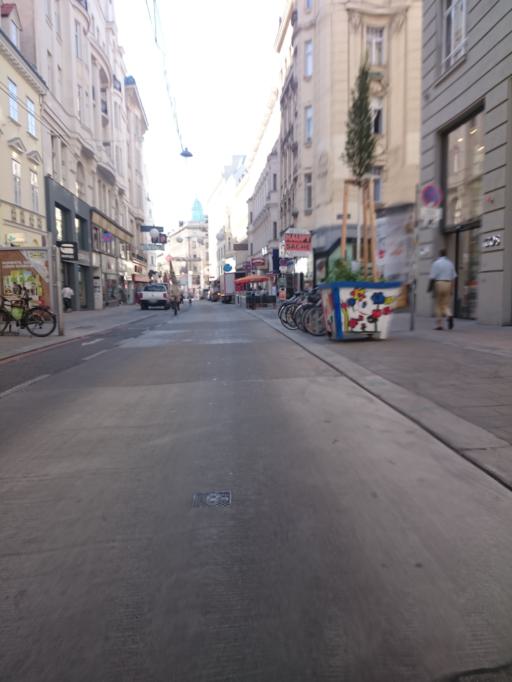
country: AT
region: Vienna
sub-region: Wien Stadt
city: Vienna
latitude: 48.1995
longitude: 16.3495
